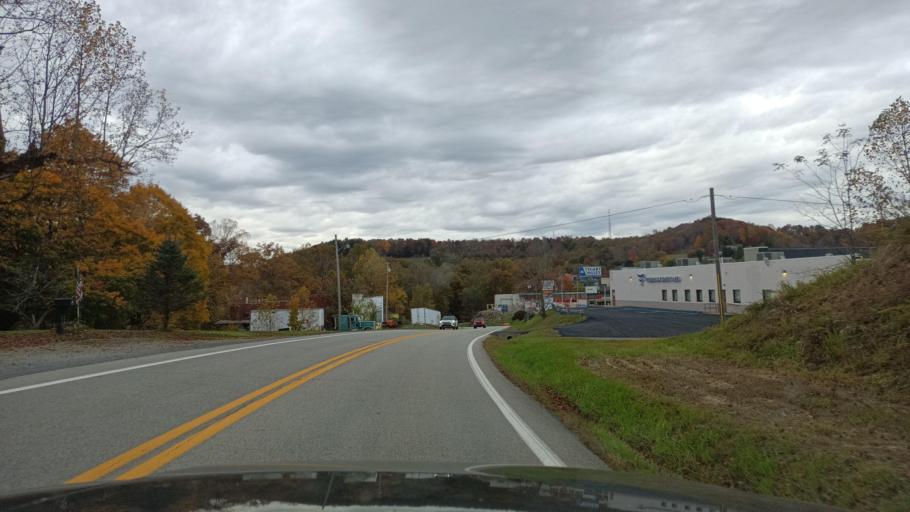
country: US
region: West Virginia
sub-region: Taylor County
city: Grafton
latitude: 39.3432
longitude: -79.9981
